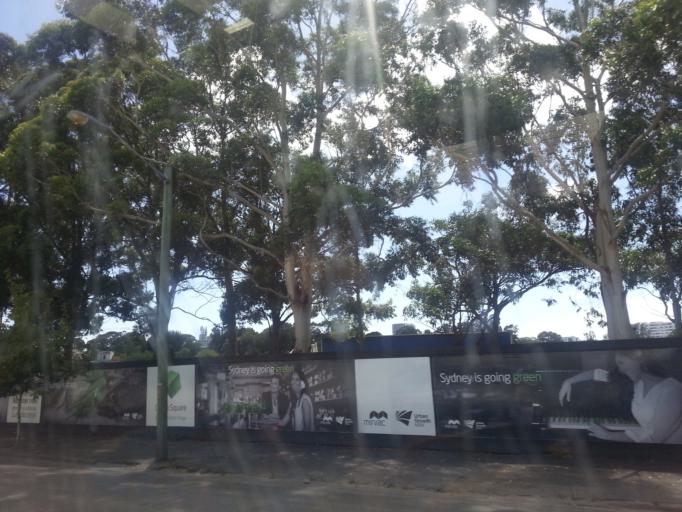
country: AU
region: New South Wales
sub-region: City of Sydney
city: Alexandria
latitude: -33.9072
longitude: 151.2028
